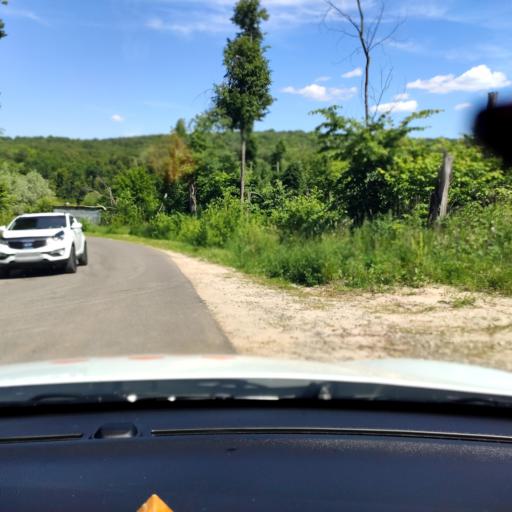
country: RU
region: Tatarstan
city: Sviyazhsk
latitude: 55.7771
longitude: 48.7882
